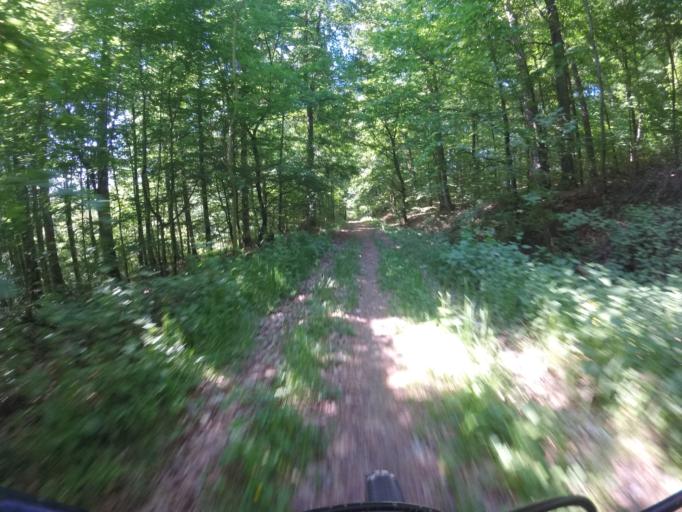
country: DE
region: Baden-Wuerttemberg
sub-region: Regierungsbezirk Stuttgart
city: Aspach
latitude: 49.0013
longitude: 9.4163
